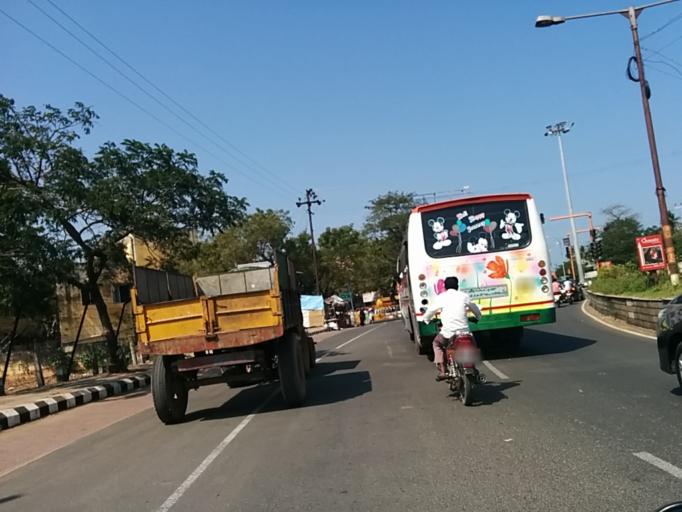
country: IN
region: Pondicherry
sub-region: Puducherry
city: Puducherry
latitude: 11.9433
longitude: 79.8084
